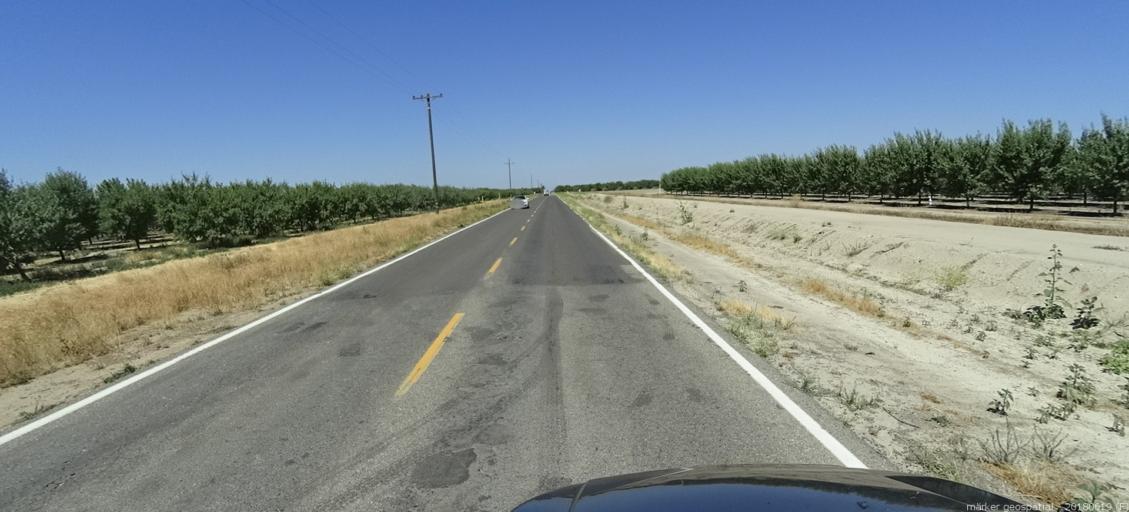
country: US
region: California
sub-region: Madera County
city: Parkwood
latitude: 36.8513
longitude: -120.1495
